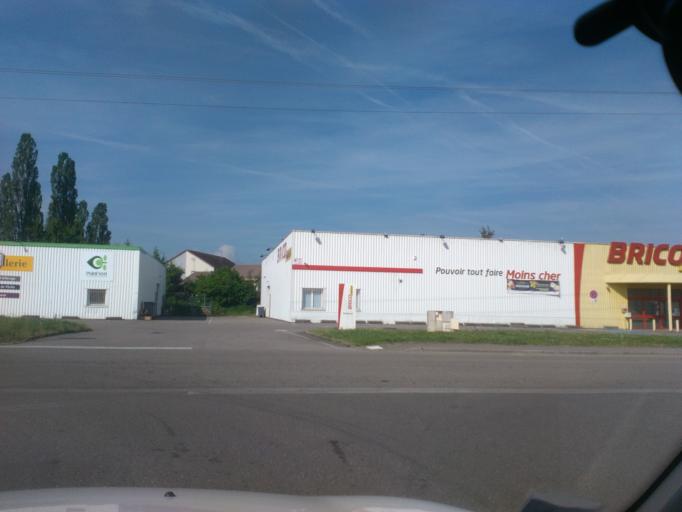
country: FR
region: Lorraine
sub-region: Departement des Vosges
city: Mirecourt
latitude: 48.3088
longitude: 6.1359
